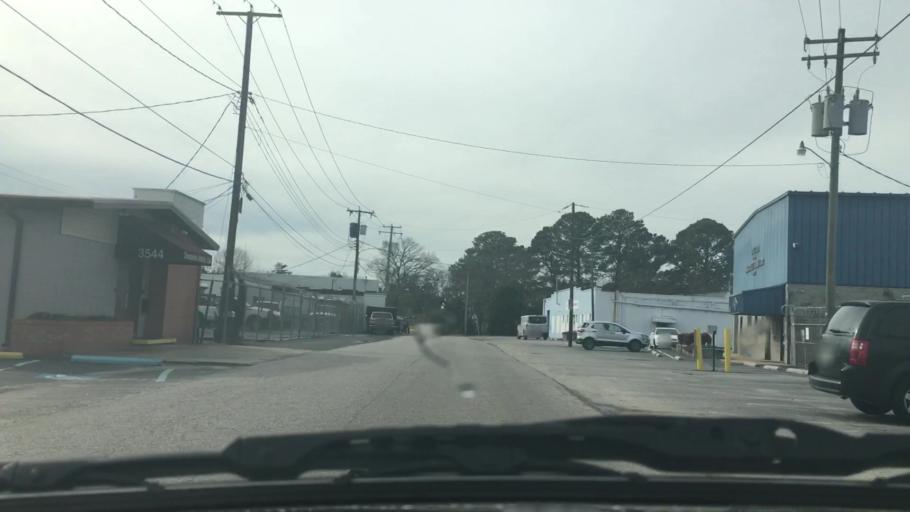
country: US
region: Virginia
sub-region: City of Norfolk
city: Norfolk
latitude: 36.8823
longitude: -76.2536
